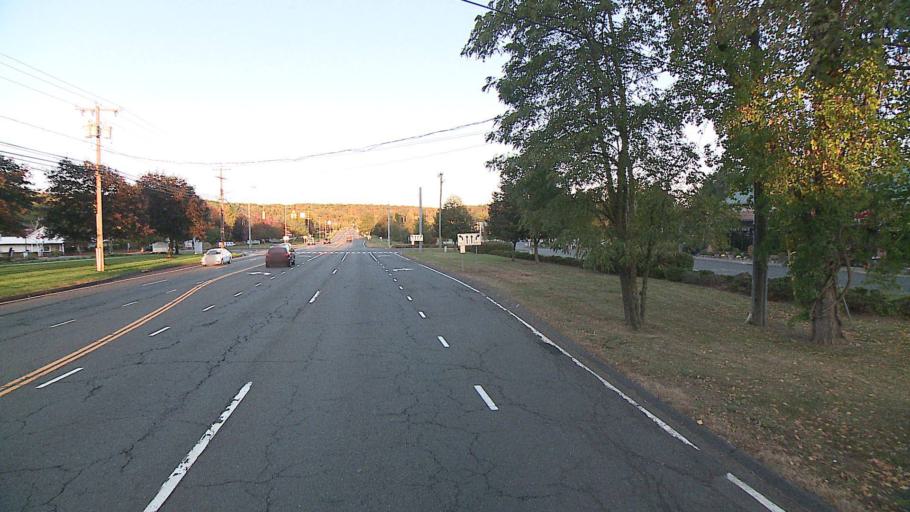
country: US
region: Connecticut
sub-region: Hartford County
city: Canton Valley
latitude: 41.8150
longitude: -72.8599
